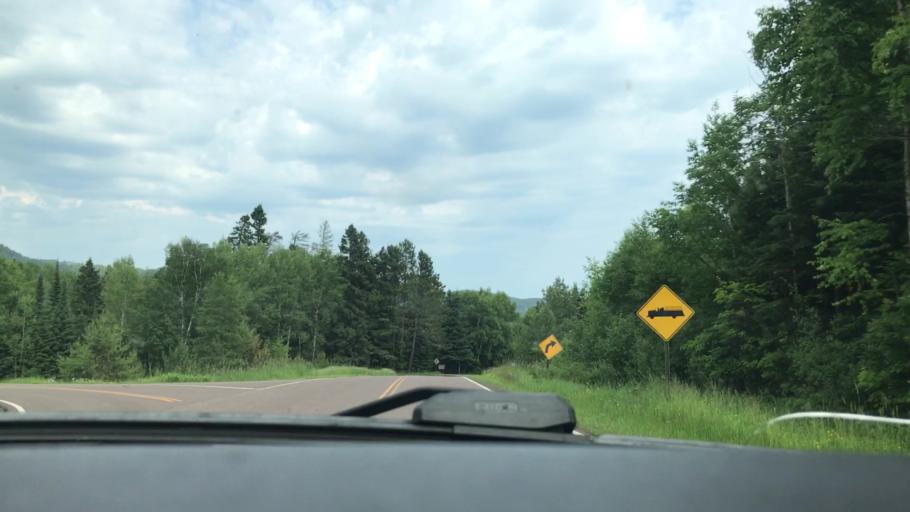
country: CA
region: Ontario
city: Neebing
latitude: 47.9646
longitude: -89.6871
